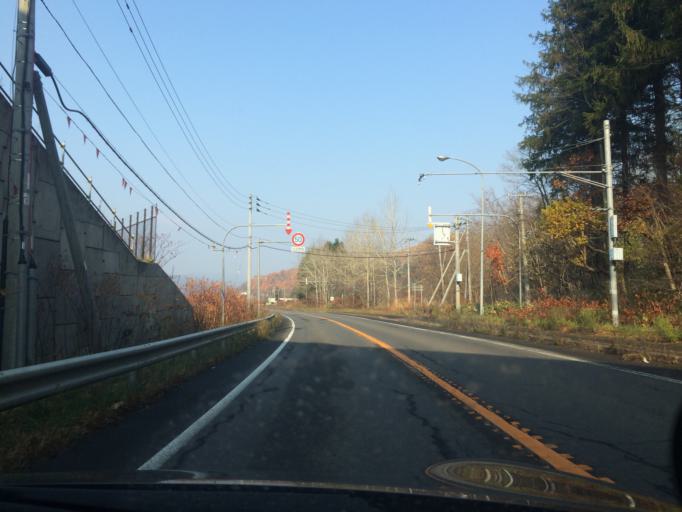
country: JP
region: Hokkaido
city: Iwamizawa
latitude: 42.9314
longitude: 142.0589
